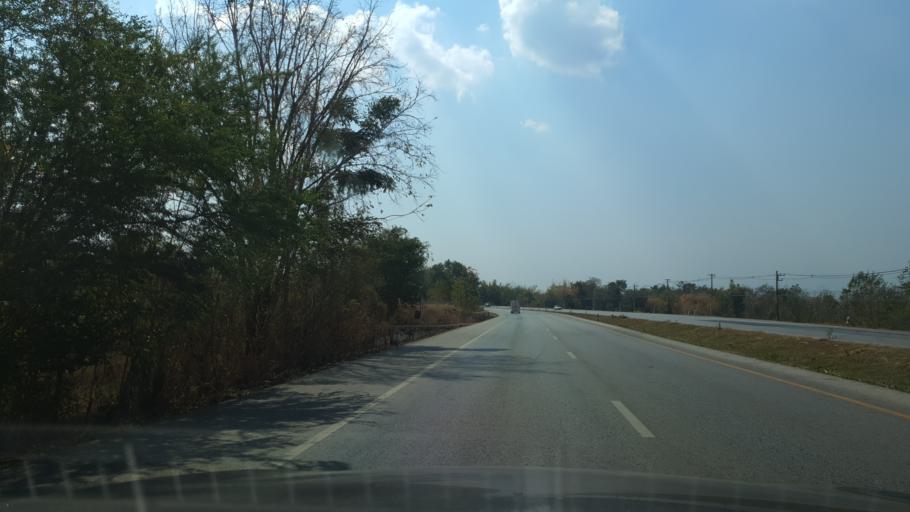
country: TH
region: Lampang
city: Mae Phrik
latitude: 17.4116
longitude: 99.1518
